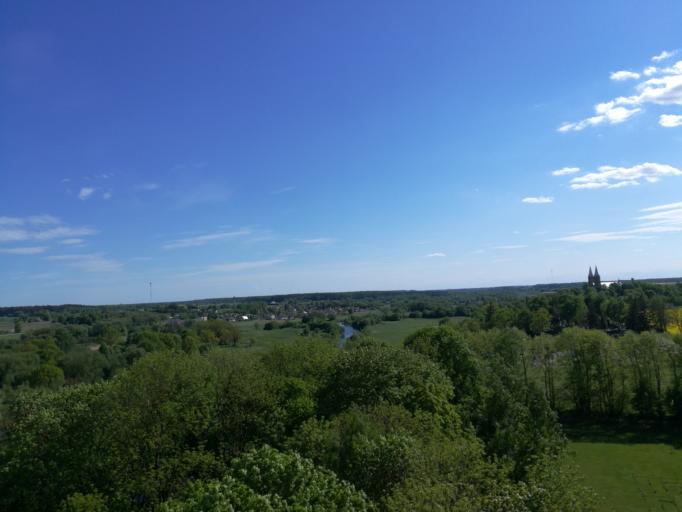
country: LT
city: Ramygala
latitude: 55.5518
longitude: 24.1055
